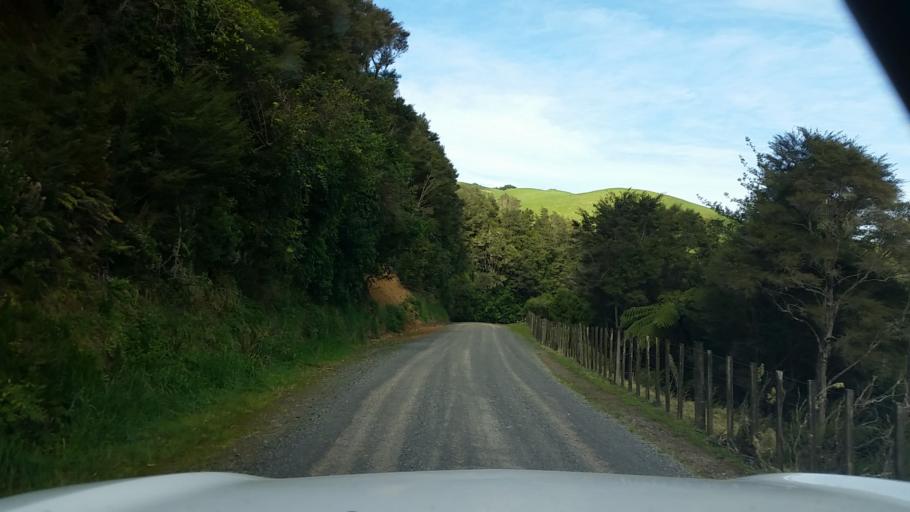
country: NZ
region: Waikato
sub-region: Hauraki District
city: Ngatea
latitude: -37.4731
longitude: 175.4568
